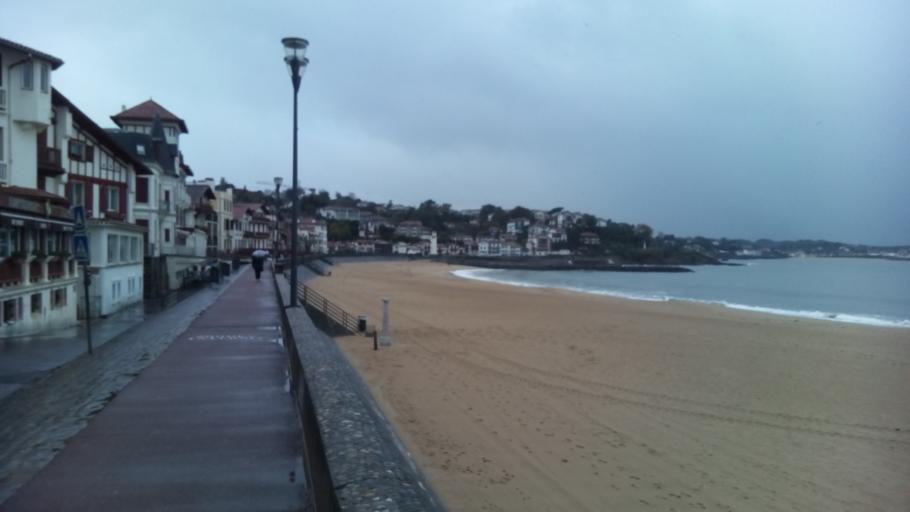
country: FR
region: Aquitaine
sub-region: Departement des Pyrenees-Atlantiques
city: Saint-Jean-de-Luz
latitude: 43.3891
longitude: -1.6639
